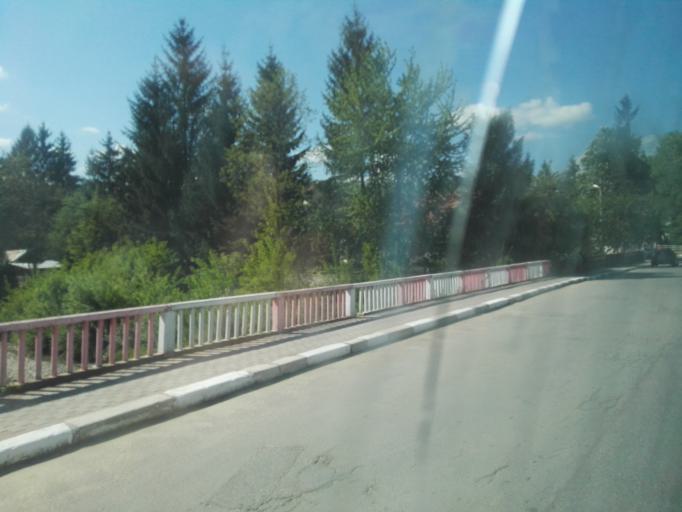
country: RO
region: Prahova
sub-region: Oras Slanic
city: Grosani
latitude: 45.2315
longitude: 25.9398
